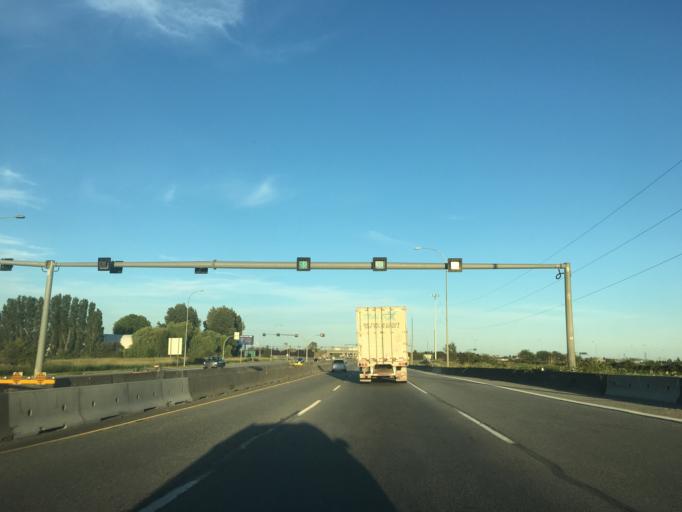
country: CA
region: British Columbia
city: Ladner
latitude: 49.1102
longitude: -123.0612
